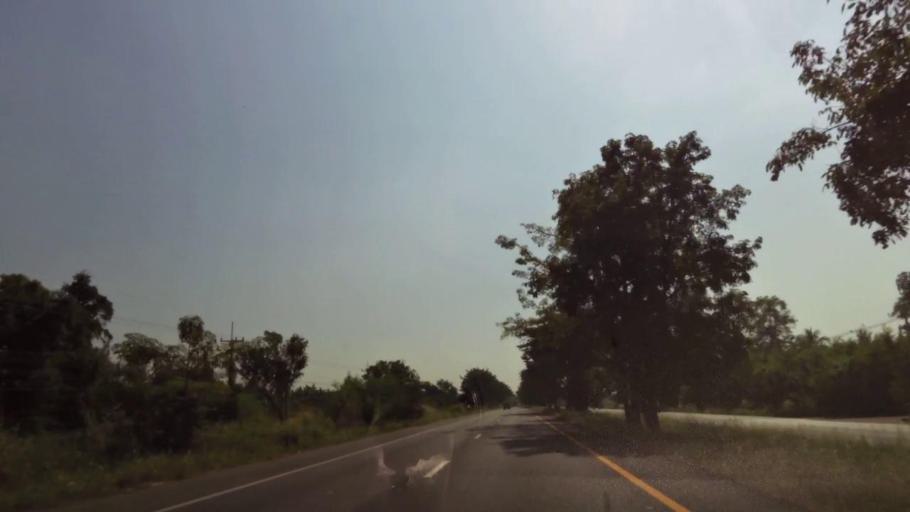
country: TH
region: Nakhon Sawan
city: Kao Liao
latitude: 15.9736
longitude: 100.1191
